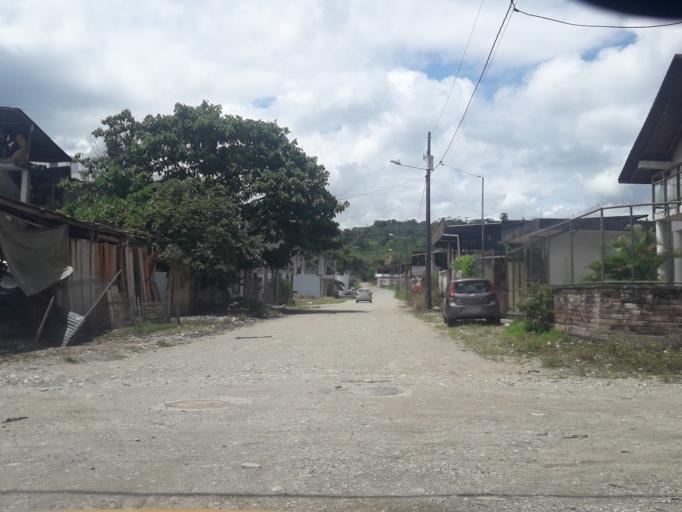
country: EC
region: Napo
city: Tena
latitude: -1.0089
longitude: -77.8157
